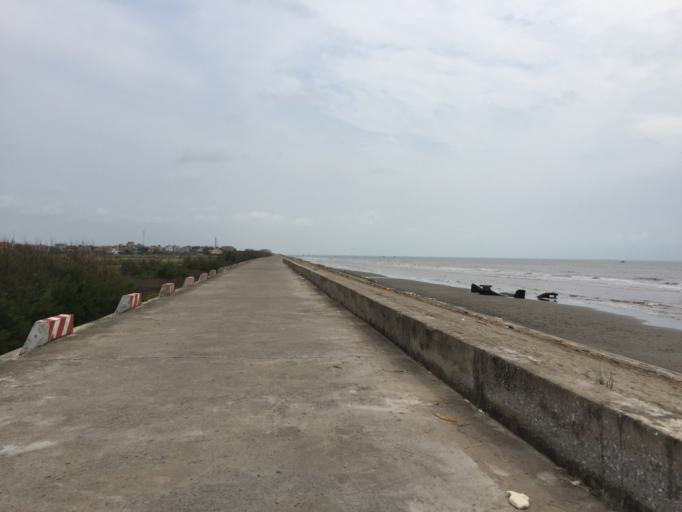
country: VN
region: Ninh Binh
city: Thi Tran Phat Diem
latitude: 20.0143
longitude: 106.2094
